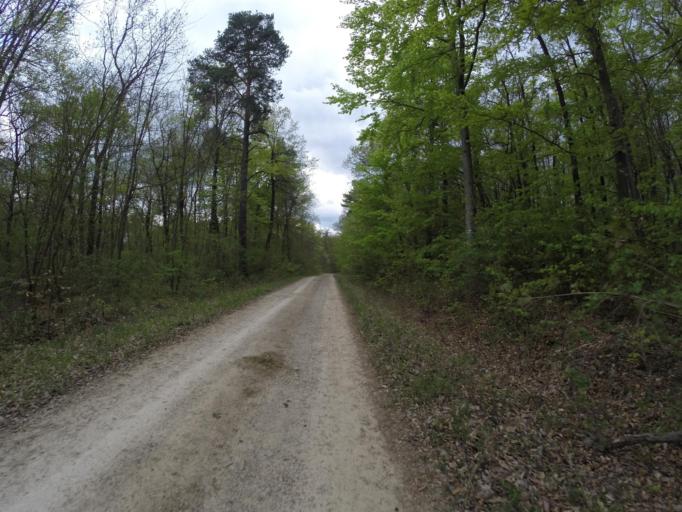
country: DE
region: Thuringia
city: Golmsdorf
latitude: 50.9494
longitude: 11.6725
